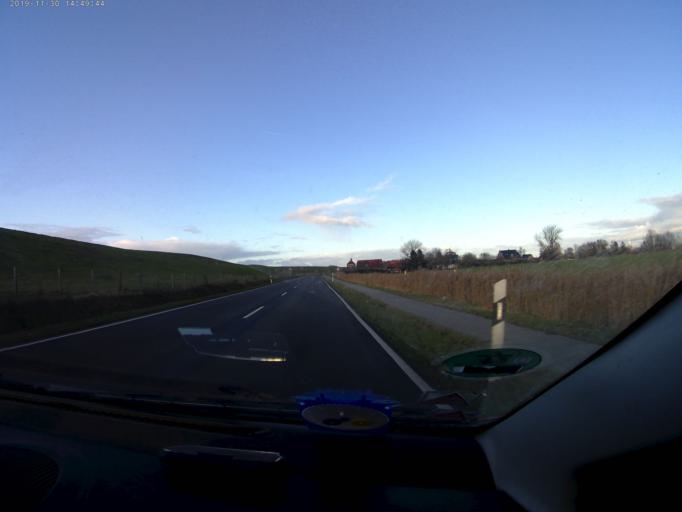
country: DE
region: Lower Saxony
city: Jemgum
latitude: 53.2508
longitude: 7.4054
